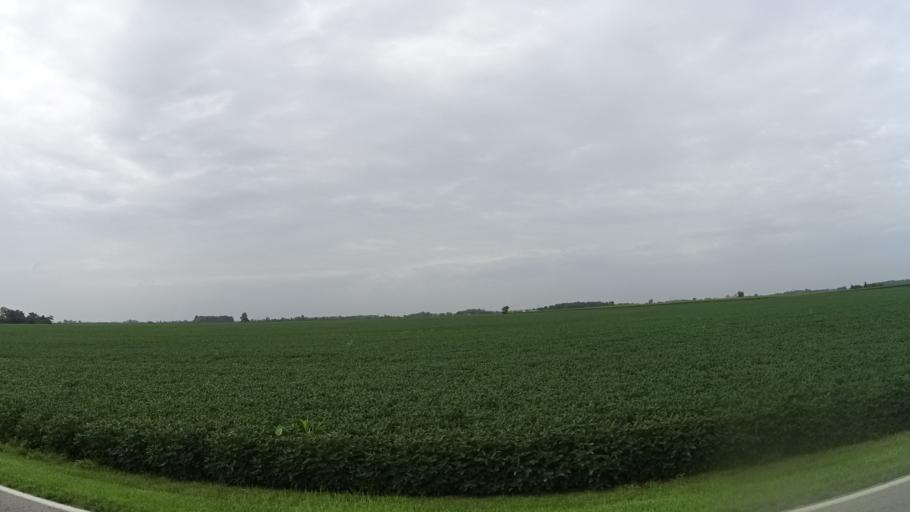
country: US
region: Indiana
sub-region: Madison County
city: Lapel
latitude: 40.0437
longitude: -85.8099
